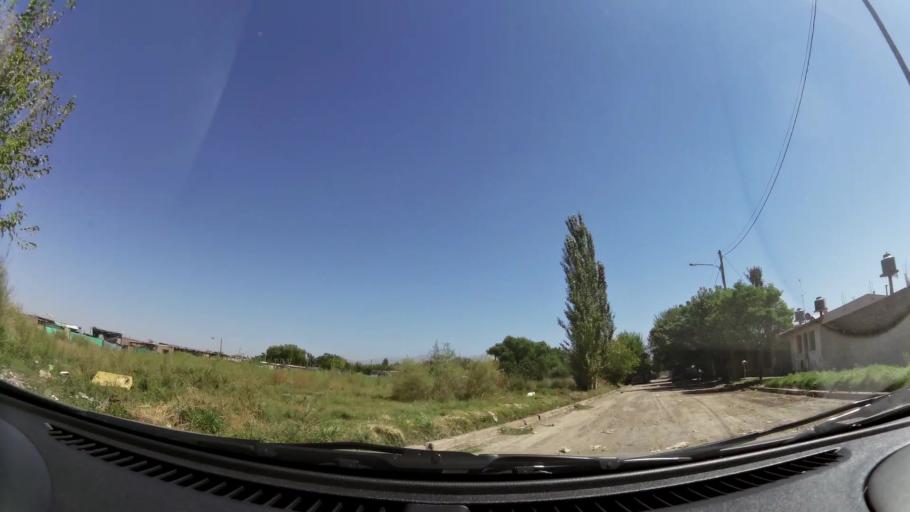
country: AR
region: Mendoza
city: Villa Nueva
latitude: -32.8744
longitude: -68.7848
